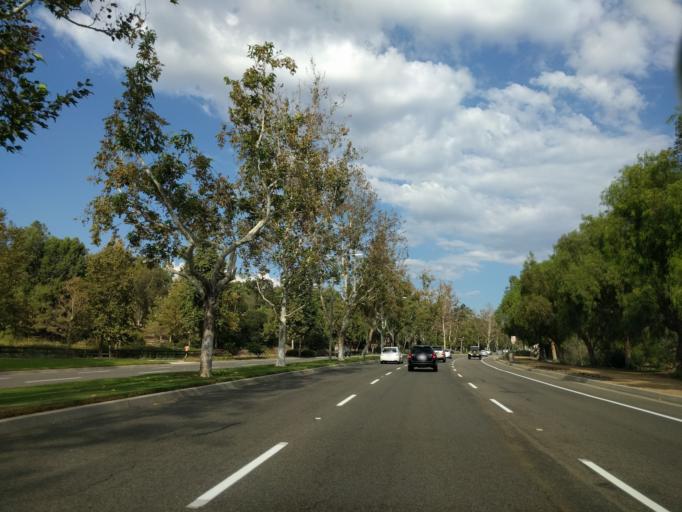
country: US
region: California
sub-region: Orange County
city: Aliso Viejo
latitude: 33.5738
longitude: -117.6976
